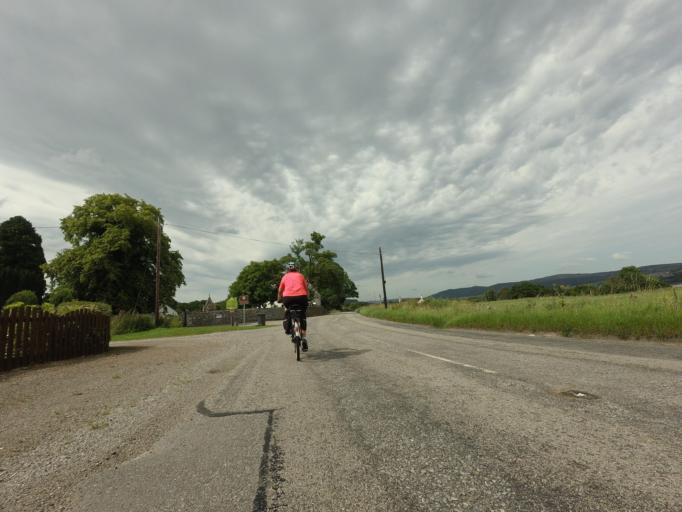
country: GB
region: Scotland
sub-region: Highland
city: Alness
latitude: 57.8721
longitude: -4.3519
